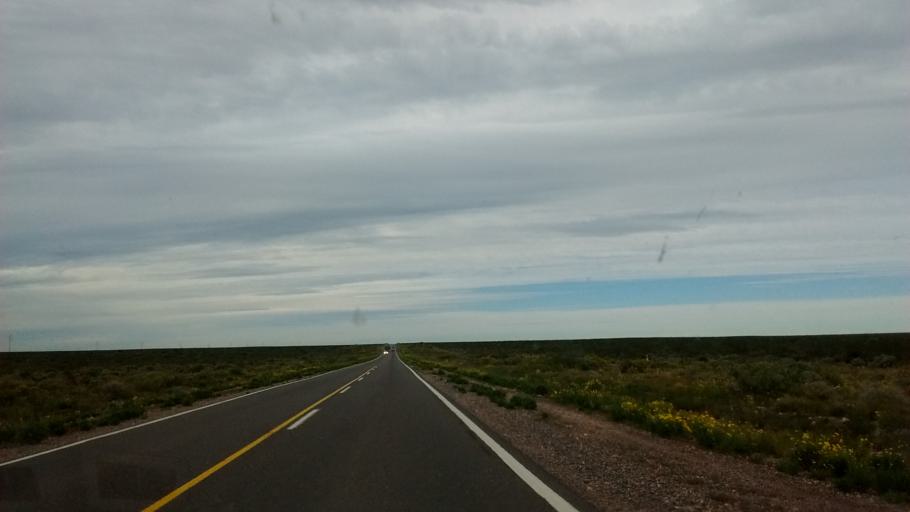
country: AR
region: Rio Negro
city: Catriel
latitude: -38.2638
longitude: -67.9909
